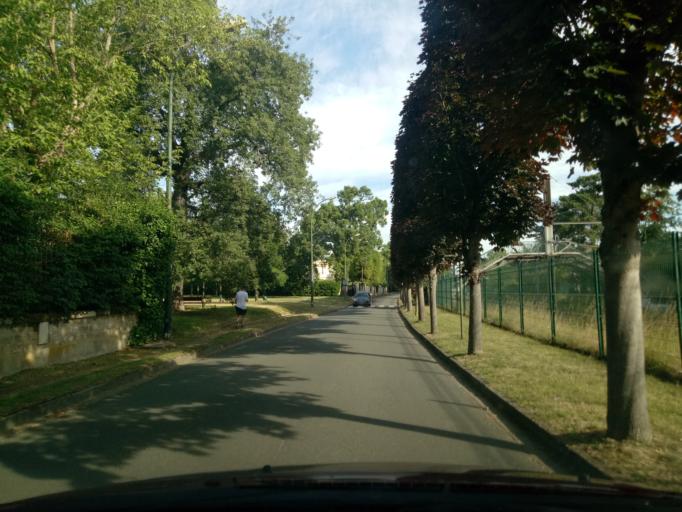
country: FR
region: Ile-de-France
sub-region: Departement des Yvelines
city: Le Vesinet
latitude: 48.8944
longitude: 2.1245
